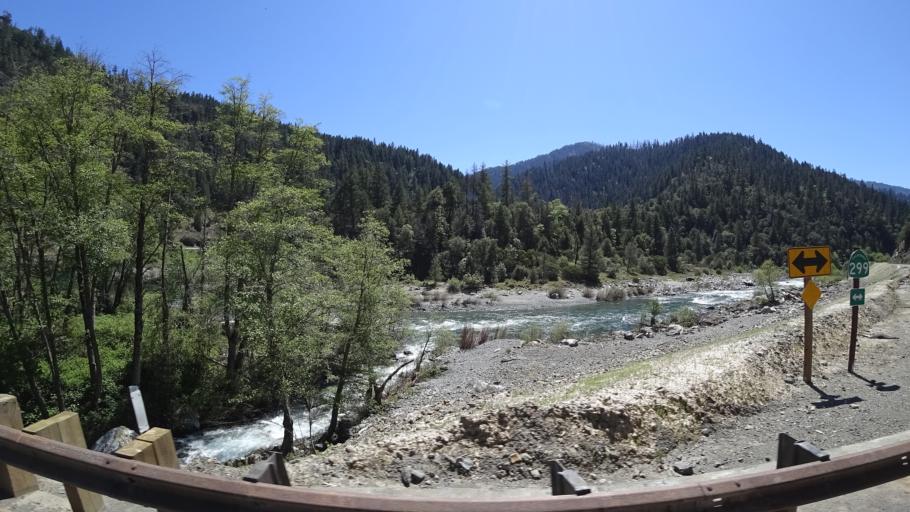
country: US
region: California
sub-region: Trinity County
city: Hayfork
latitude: 40.7798
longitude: -123.3100
